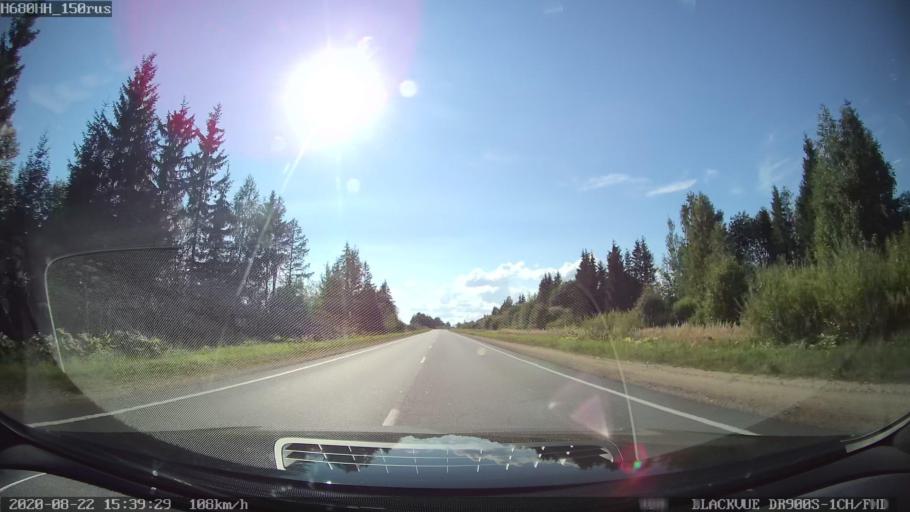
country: RU
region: Tverskaya
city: Bezhetsk
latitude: 57.7570
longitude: 36.6233
